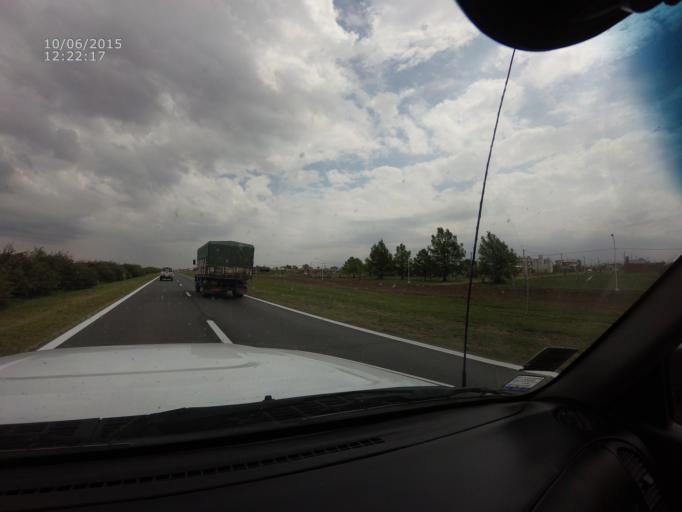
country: AR
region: Santa Fe
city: Roldan
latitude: -32.9184
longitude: -60.9336
